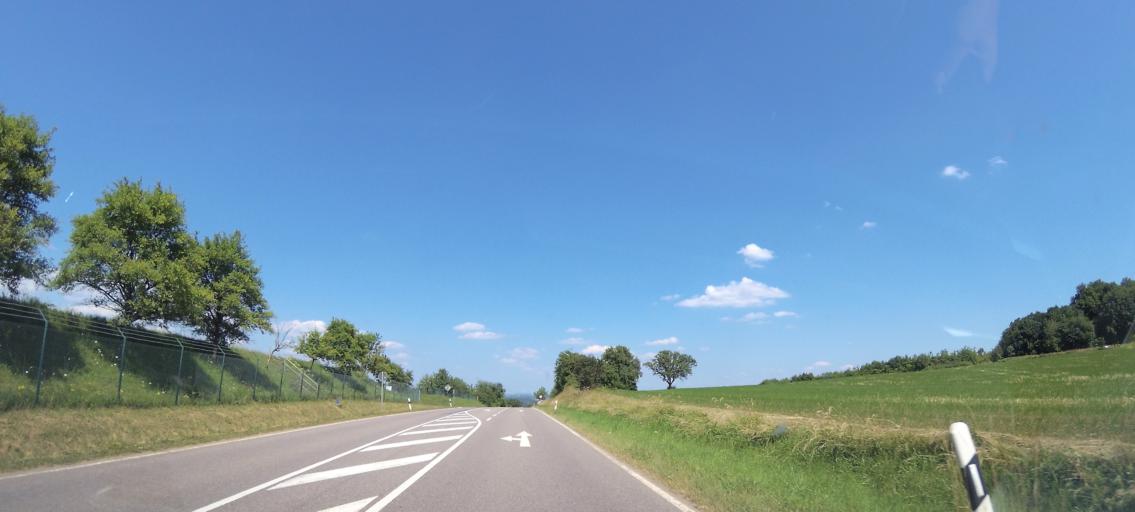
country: DE
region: Saarland
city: Mettlach
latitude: 49.4376
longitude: 6.5799
